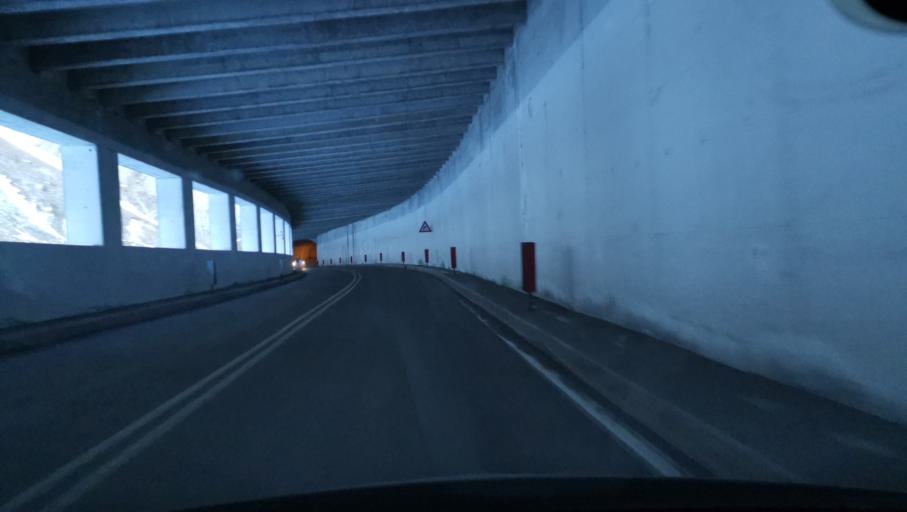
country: IT
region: Piedmont
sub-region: Provincia di Cuneo
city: Pietraporzio
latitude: 44.3585
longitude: 7.0036
